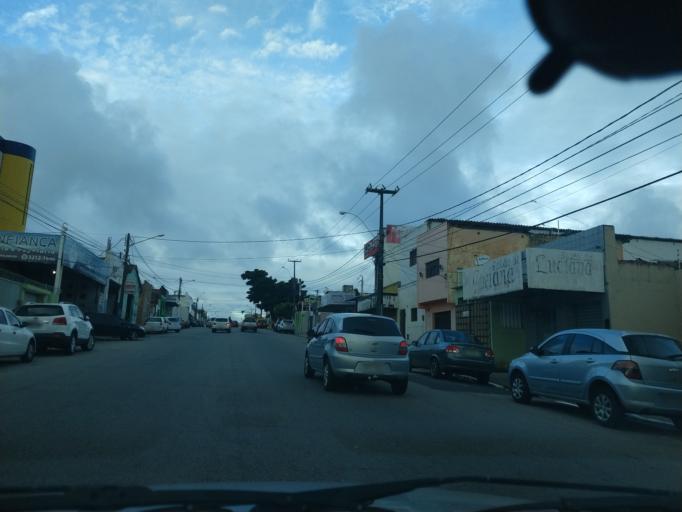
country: BR
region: Rio Grande do Norte
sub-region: Natal
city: Natal
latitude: -5.8003
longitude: -35.2221
